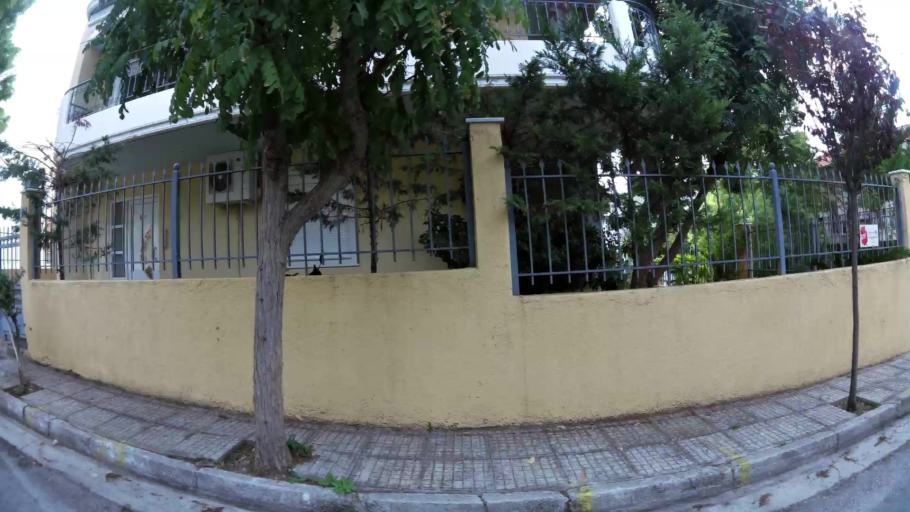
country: GR
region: Attica
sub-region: Nomarchia Athinas
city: Kamateron
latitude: 38.0525
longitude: 23.7015
